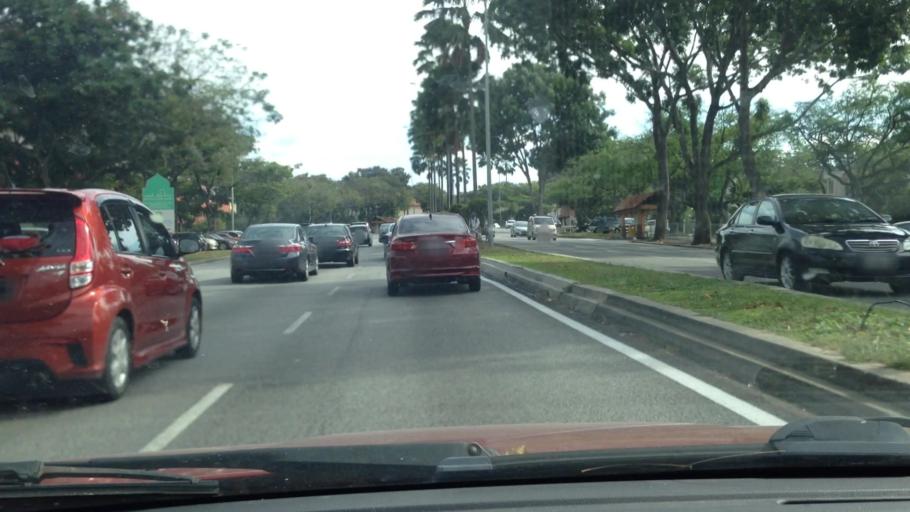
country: MY
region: Selangor
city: Subang Jaya
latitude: 3.0662
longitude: 101.5802
